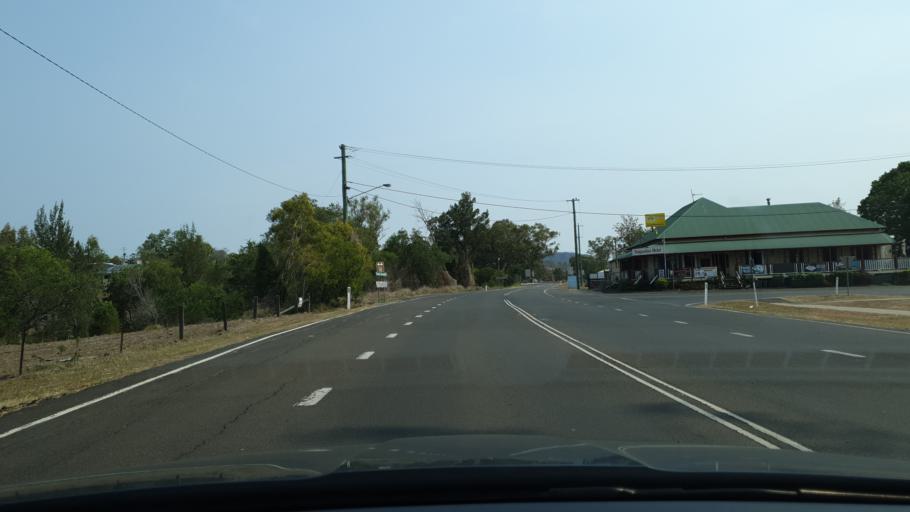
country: AU
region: Queensland
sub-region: Ipswich
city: Deebing Heights
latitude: -28.0038
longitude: 152.6812
